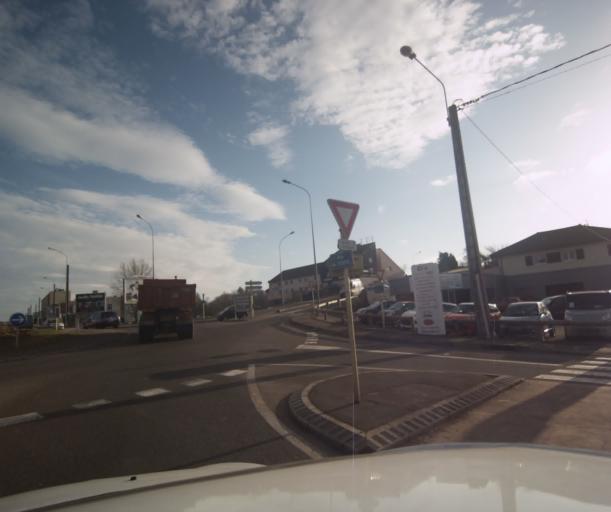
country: FR
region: Franche-Comte
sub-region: Departement du Doubs
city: Besancon
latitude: 47.2599
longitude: 6.0085
